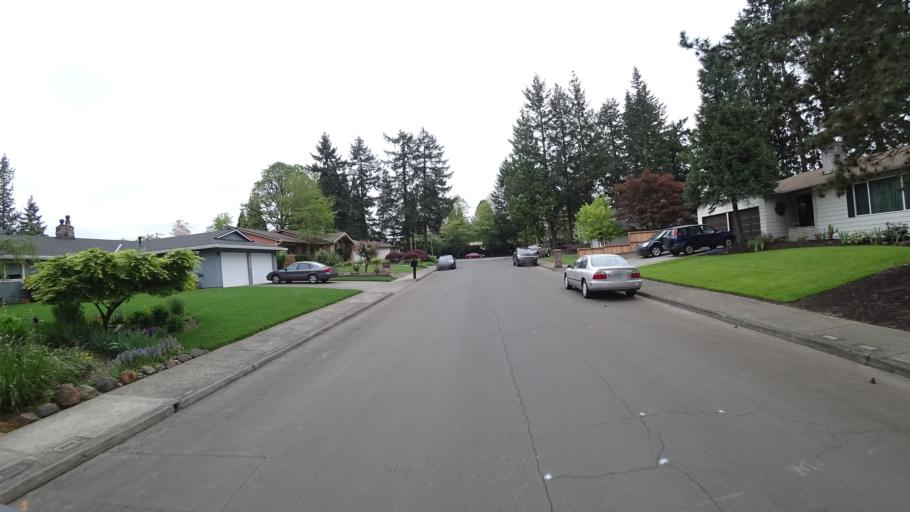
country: US
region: Oregon
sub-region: Washington County
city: Aloha
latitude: 45.5100
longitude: -122.8686
